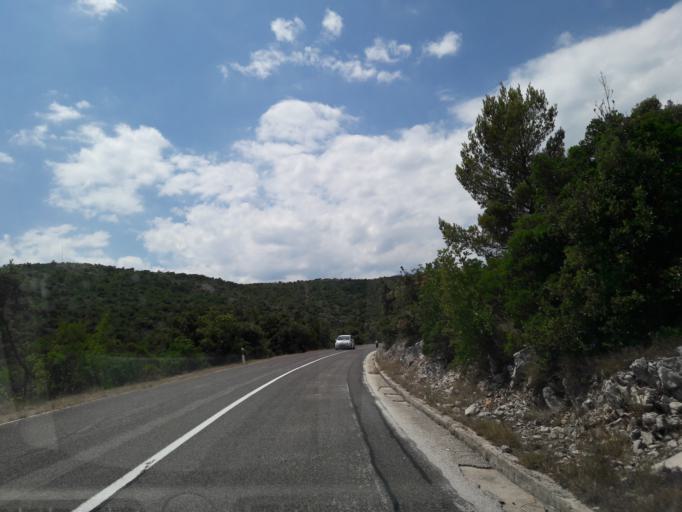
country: HR
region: Dubrovacko-Neretvanska
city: Orebic
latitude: 42.9686
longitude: 17.2883
